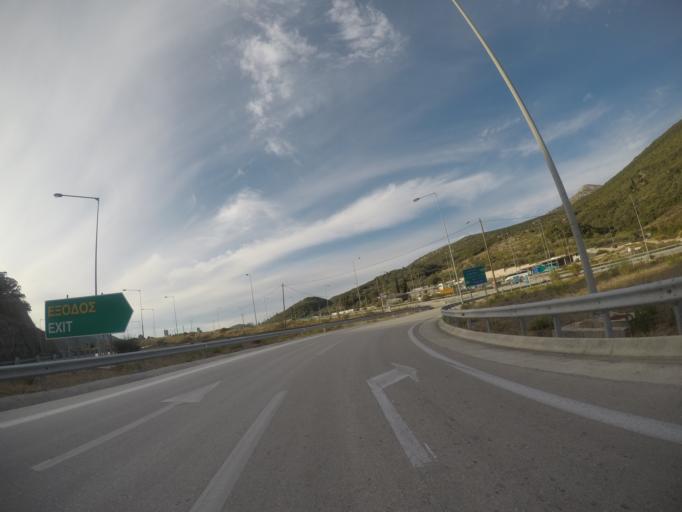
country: GR
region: Epirus
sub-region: Nomos Thesprotias
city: Plataria
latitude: 39.4507
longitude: 20.3592
